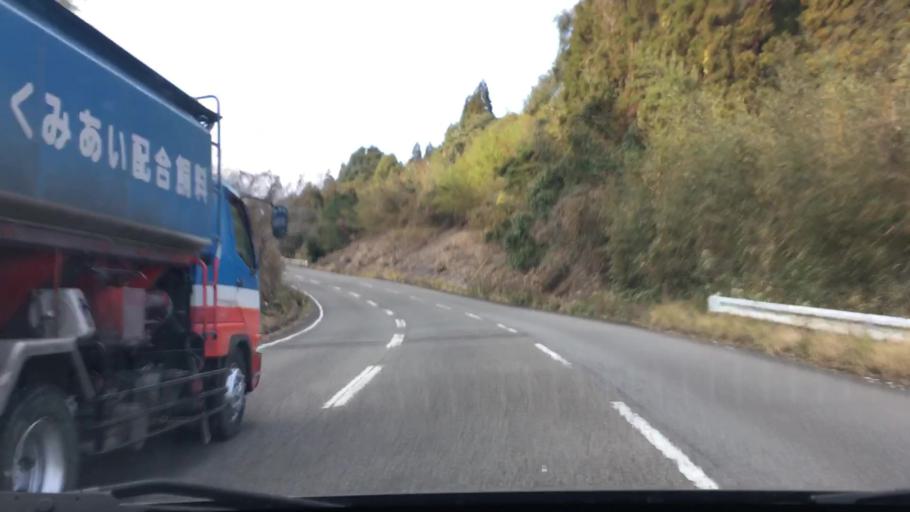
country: JP
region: Miyazaki
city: Nichinan
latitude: 31.6340
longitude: 131.3388
